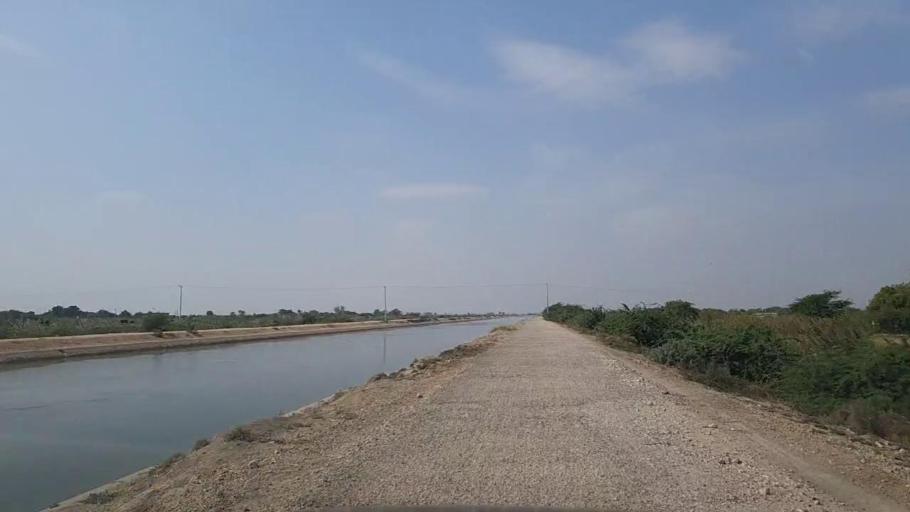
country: PK
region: Sindh
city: Thatta
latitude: 24.7528
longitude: 67.7675
